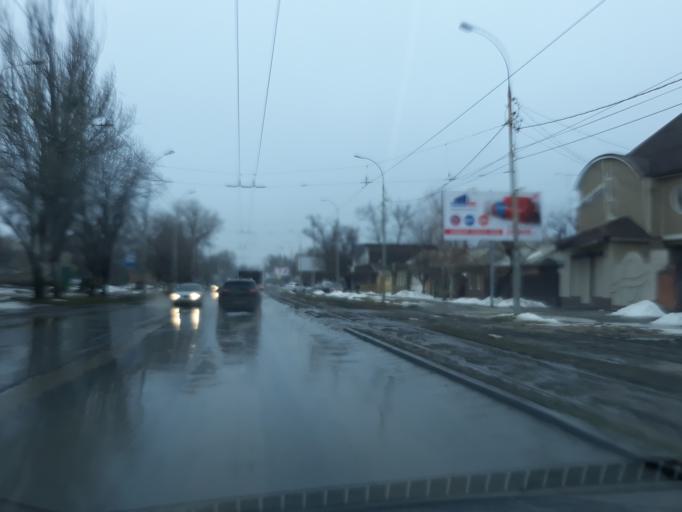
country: RU
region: Rostov
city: Taganrog
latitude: 47.2306
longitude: 38.9181
